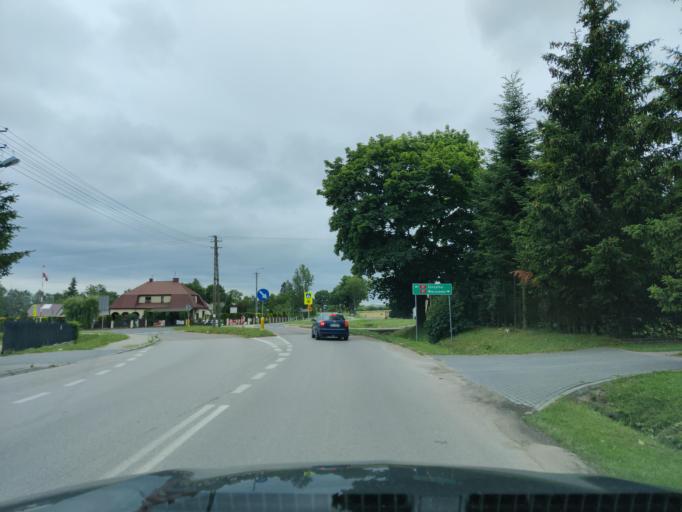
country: PL
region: Masovian Voivodeship
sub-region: Powiat pultuski
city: Pultusk
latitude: 52.7595
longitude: 21.0667
